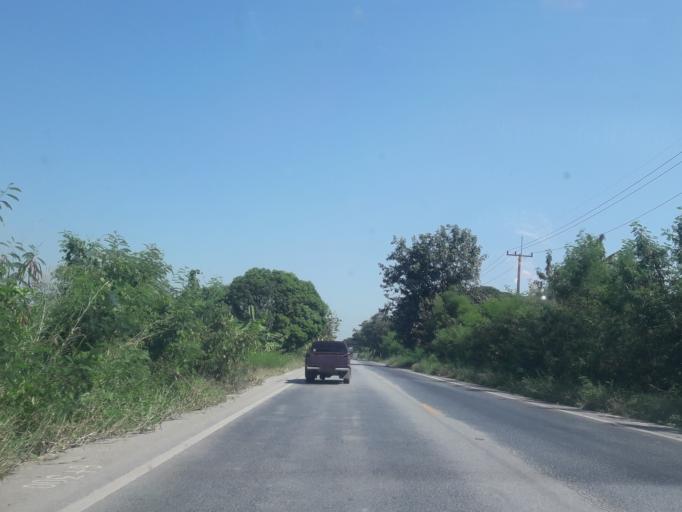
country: TH
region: Sara Buri
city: Nong Khae
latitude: 14.2940
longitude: 100.8362
